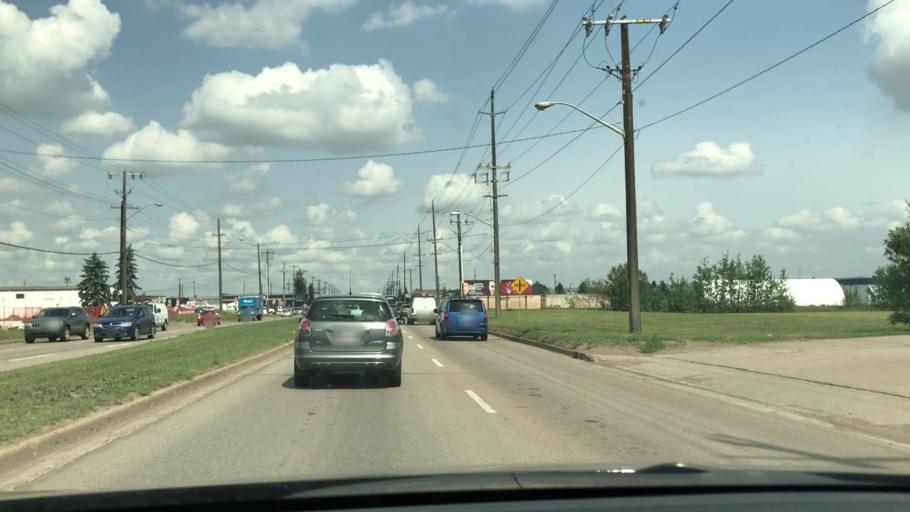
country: CA
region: Alberta
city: Edmonton
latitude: 53.5055
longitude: -113.4182
